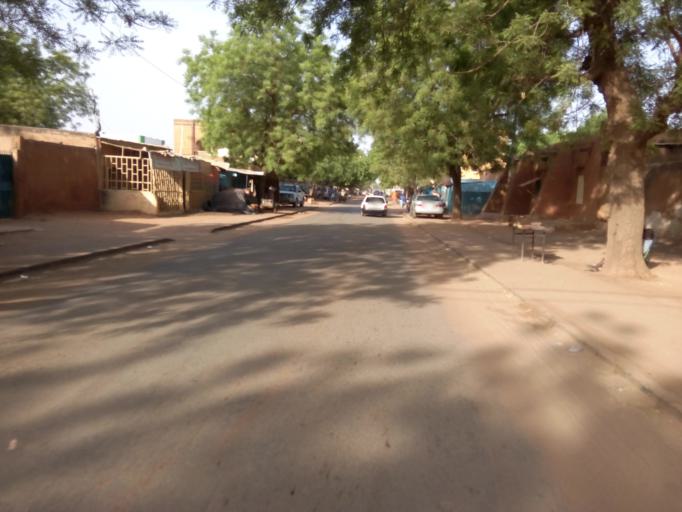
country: NE
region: Niamey
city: Niamey
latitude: 13.5126
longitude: 2.1229
